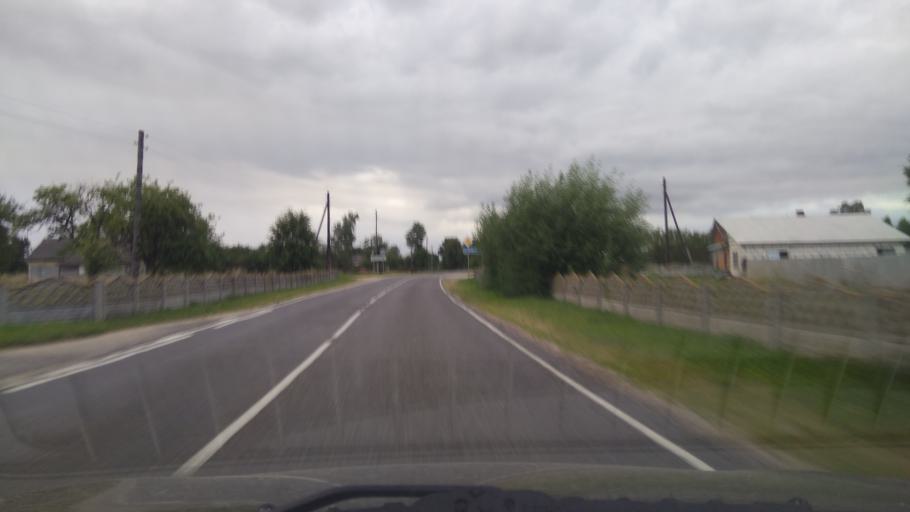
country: BY
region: Brest
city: Byaroza
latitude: 52.4213
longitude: 24.9808
